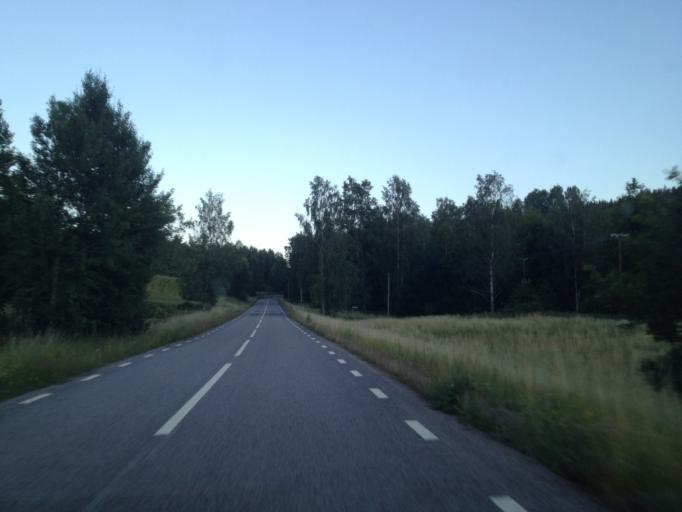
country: SE
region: Kalmar
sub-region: Vasterviks Kommun
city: Overum
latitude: 58.0087
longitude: 16.1727
